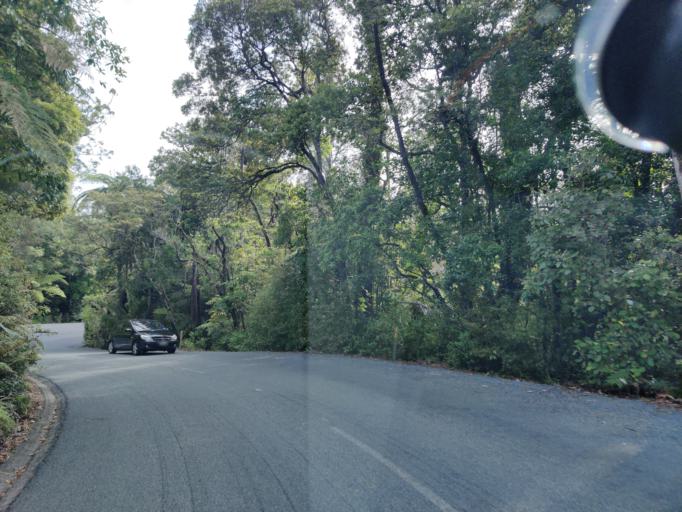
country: NZ
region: Northland
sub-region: Kaipara District
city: Dargaville
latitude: -35.6422
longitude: 173.5602
